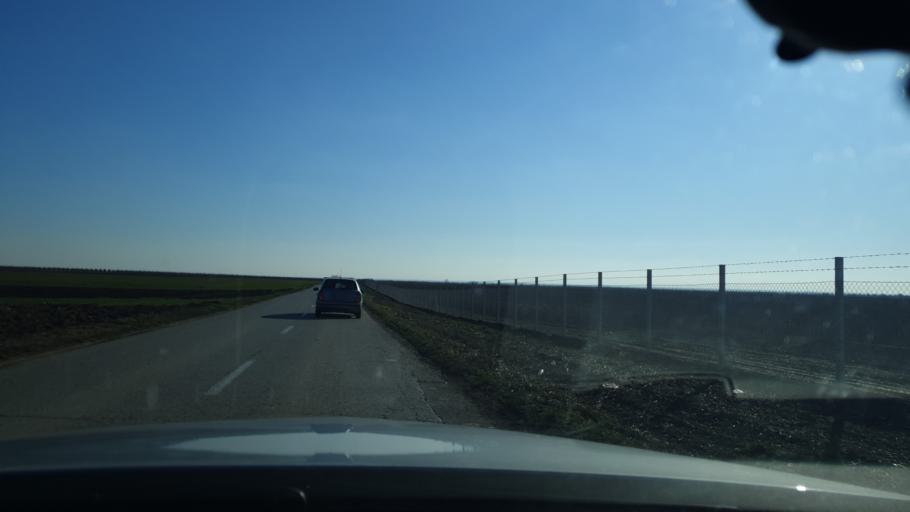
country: RS
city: Vrdnik
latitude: 45.0680
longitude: 19.8090
